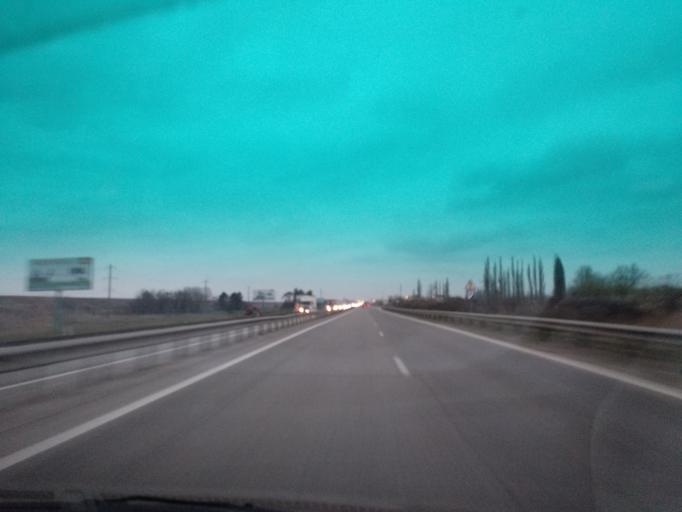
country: RU
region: Adygeya
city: Tlyustenkhabl'
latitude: 44.9302
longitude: 39.1379
